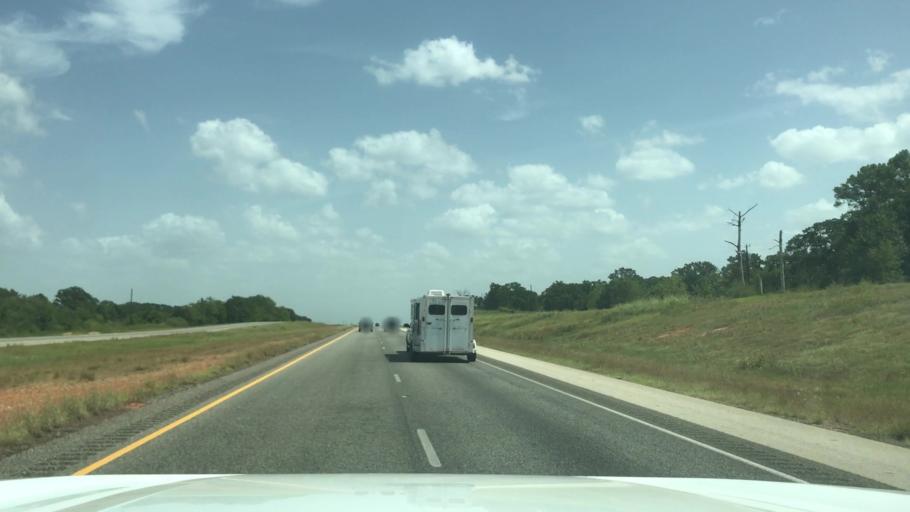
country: US
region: Texas
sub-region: Robertson County
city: Hearne
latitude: 30.9267
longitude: -96.6293
